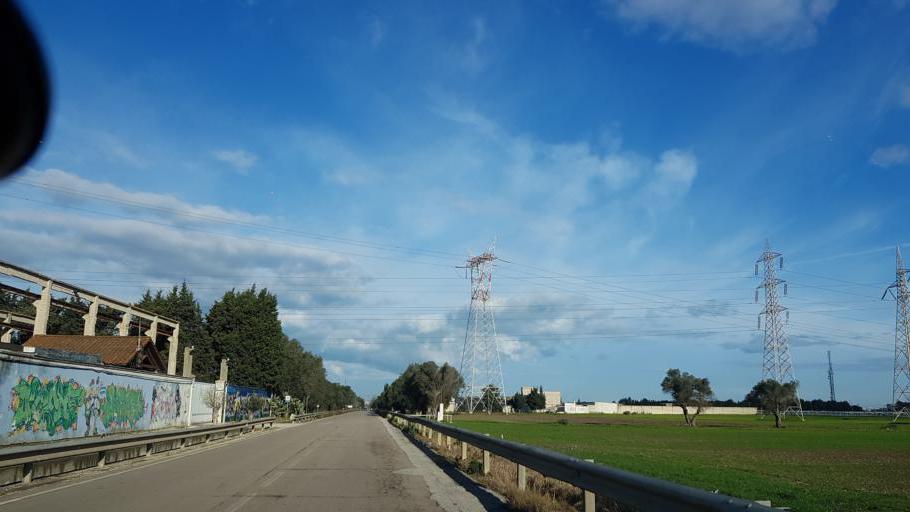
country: IT
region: Apulia
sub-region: Provincia di Brindisi
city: La Rosa
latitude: 40.6026
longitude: 17.9564
